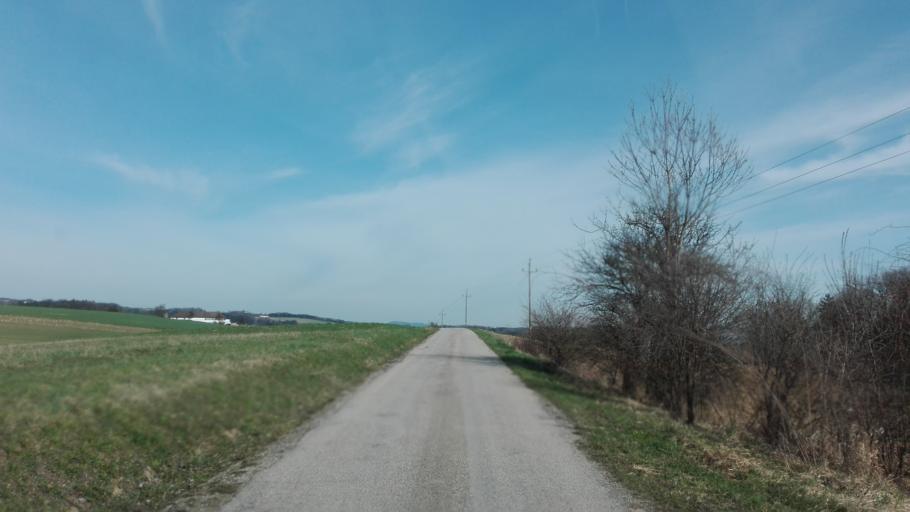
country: AT
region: Upper Austria
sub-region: Politischer Bezirk Perg
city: Perg
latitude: 48.2369
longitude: 14.6735
